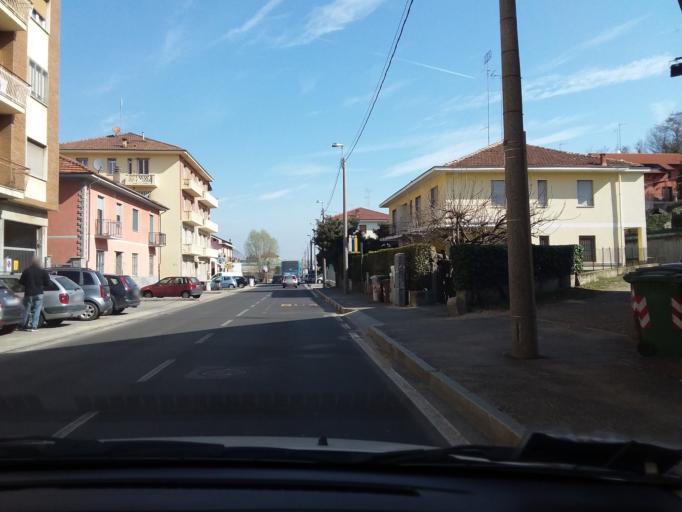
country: IT
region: Piedmont
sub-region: Provincia di Torino
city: Rivoli
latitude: 45.0819
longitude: 7.5185
